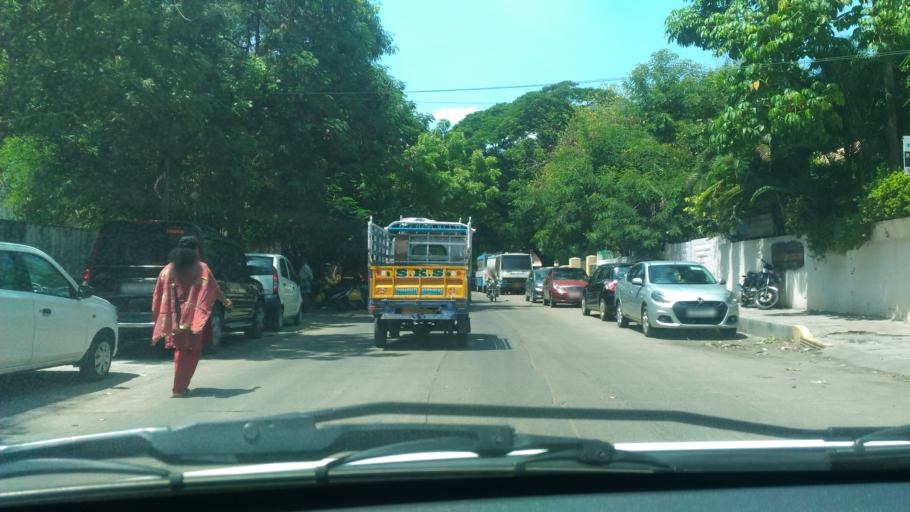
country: IN
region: Tamil Nadu
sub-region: Chennai
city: Chetput
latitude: 13.0504
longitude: 80.2456
